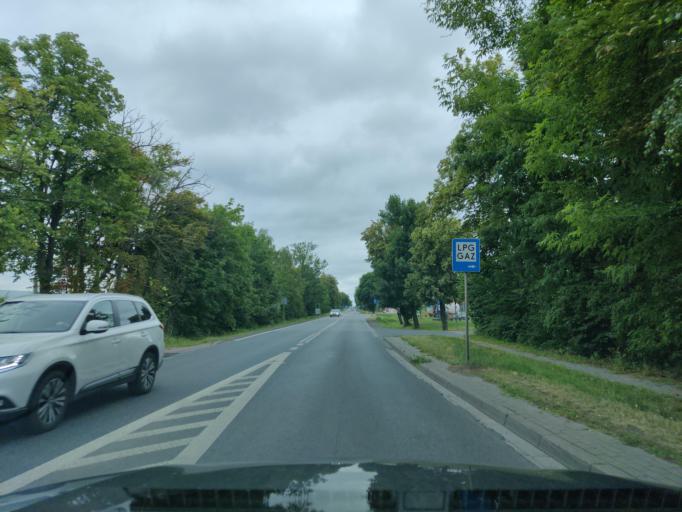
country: PL
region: Masovian Voivodeship
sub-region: Powiat pultuski
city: Pultusk
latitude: 52.6896
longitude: 21.0805
